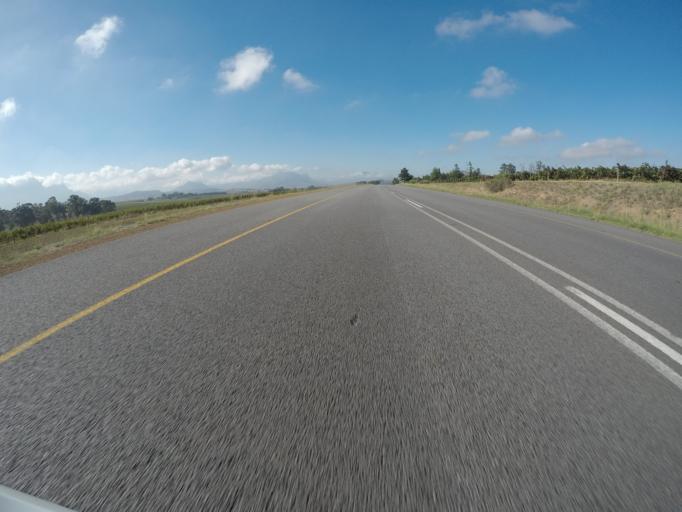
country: ZA
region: Western Cape
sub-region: Cape Winelands District Municipality
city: Stellenbosch
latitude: -33.8605
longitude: 18.8107
